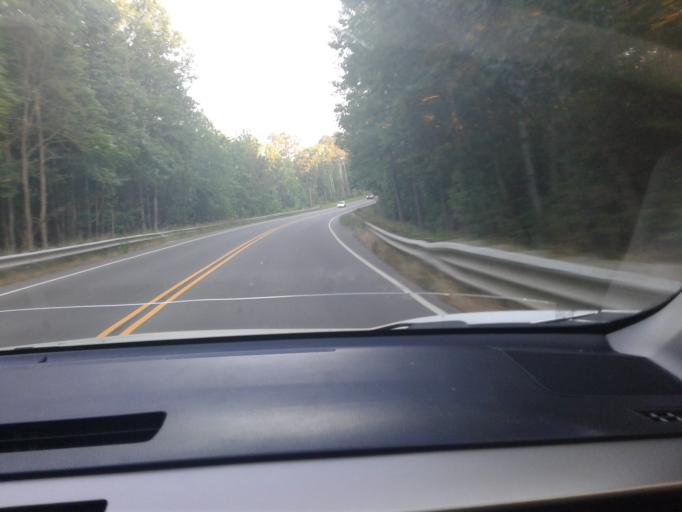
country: US
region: North Carolina
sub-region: Harnett County
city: Lillington
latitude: 35.4284
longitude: -78.8239
